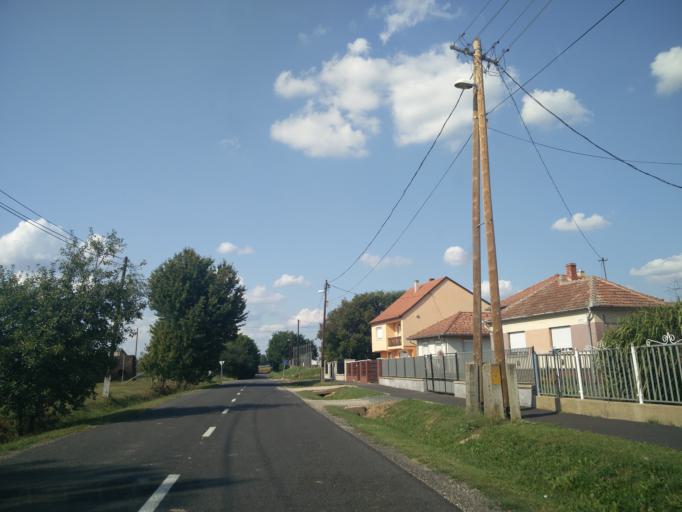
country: HU
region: Zala
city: Zalaegerszeg
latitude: 46.8789
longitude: 16.8254
